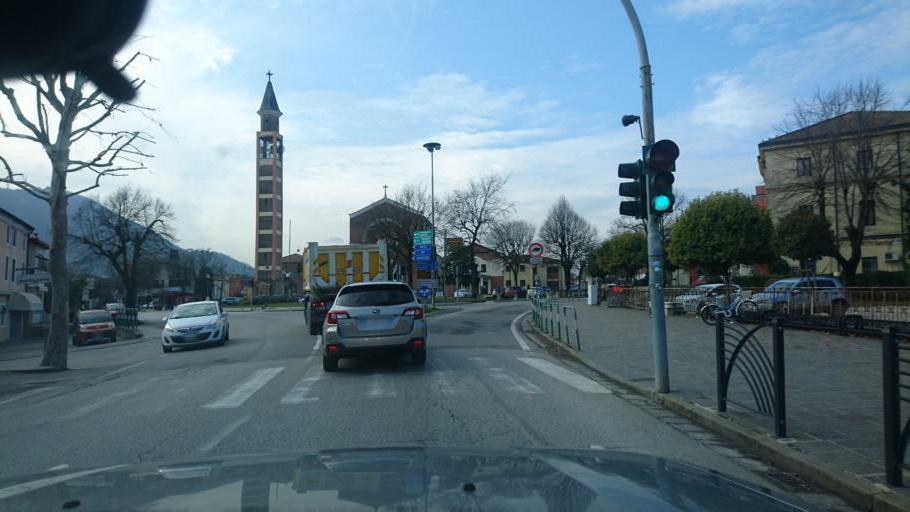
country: IT
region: Veneto
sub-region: Provincia di Padova
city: Bastia
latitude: 45.3860
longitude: 11.6529
